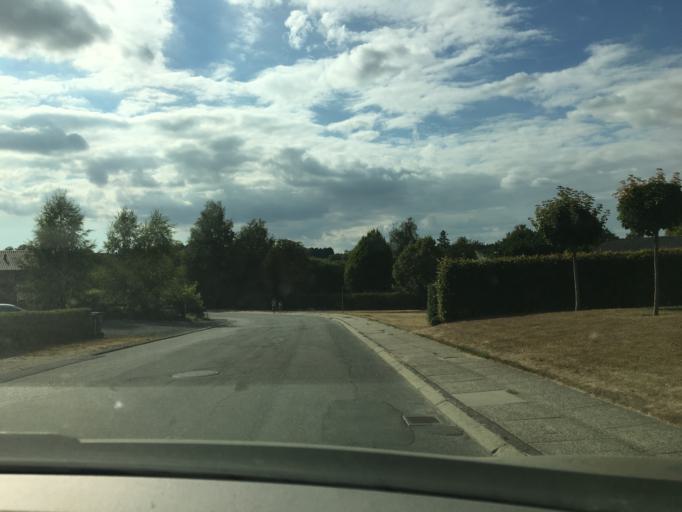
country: DK
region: South Denmark
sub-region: Nordfyns Kommune
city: Sonderso
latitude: 55.4444
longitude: 10.1906
